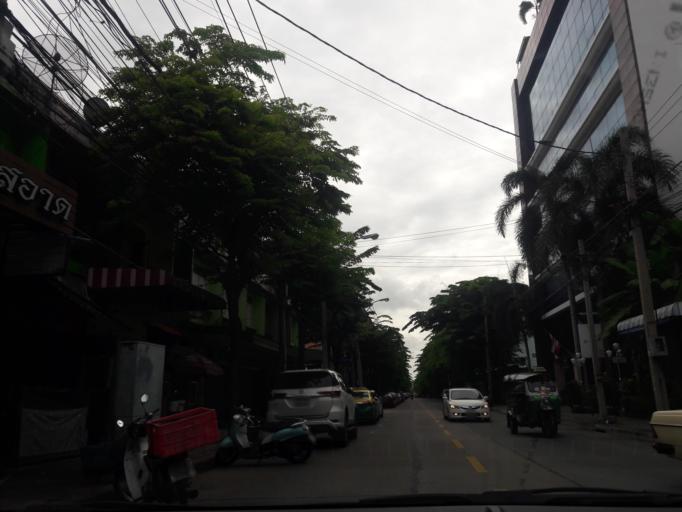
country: TH
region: Bangkok
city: Khlong San
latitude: 13.7264
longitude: 100.4995
